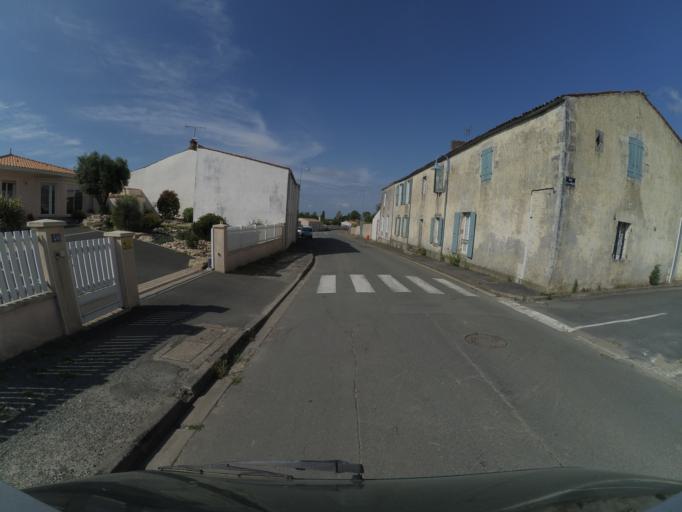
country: FR
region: Poitou-Charentes
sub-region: Departement de la Charente-Maritime
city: Andilly
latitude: 46.2424
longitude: -1.0658
